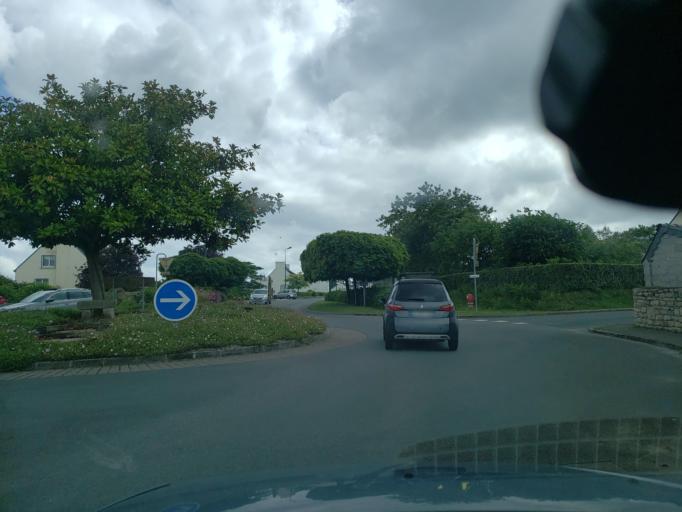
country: FR
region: Brittany
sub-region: Departement du Finistere
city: Plomeur
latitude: 47.8623
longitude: -4.2805
